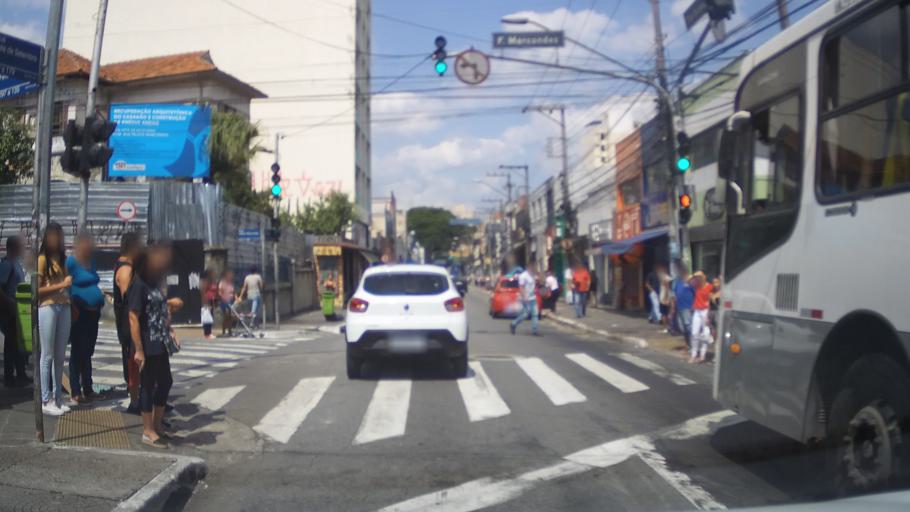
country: BR
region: Sao Paulo
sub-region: Guarulhos
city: Guarulhos
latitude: -23.4691
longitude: -46.5300
